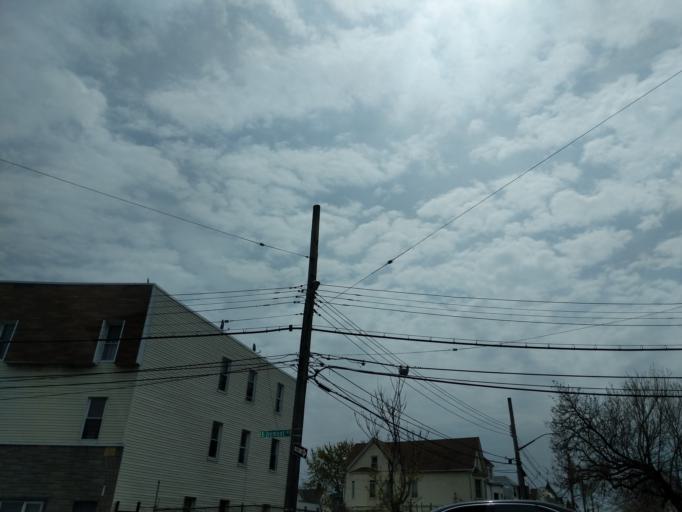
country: US
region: New York
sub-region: Bronx
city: The Bronx
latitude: 40.8398
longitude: -73.8692
